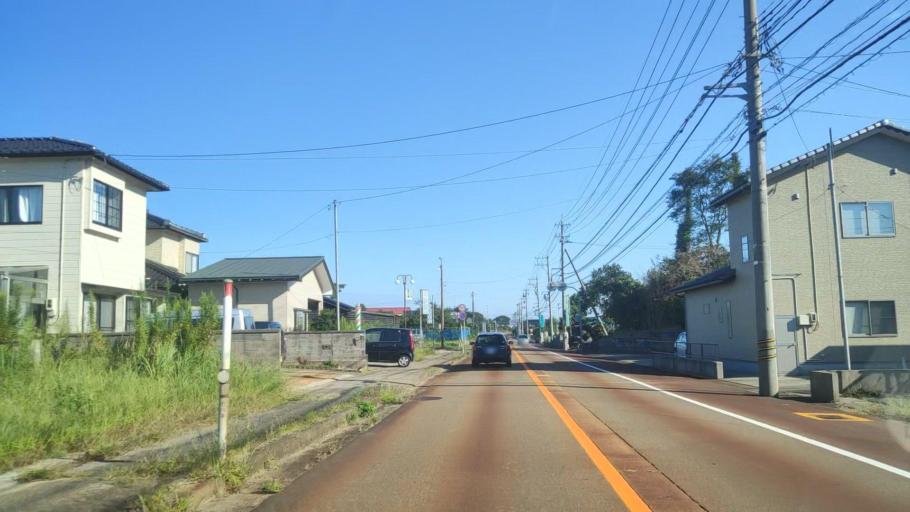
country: JP
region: Ishikawa
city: Hakui
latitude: 36.8543
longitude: 136.7694
